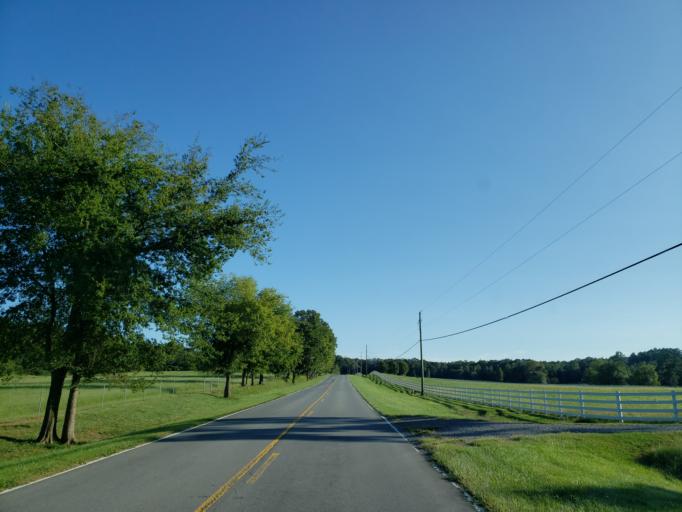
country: US
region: Georgia
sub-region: Bartow County
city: Rydal
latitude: 34.3112
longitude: -84.7741
